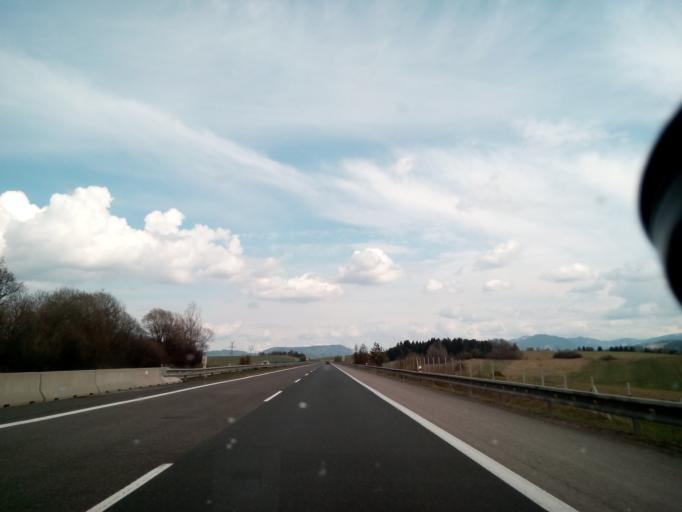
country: SK
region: Zilinsky
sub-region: Okres Zilina
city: Liptovsky Hradok
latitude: 49.0552
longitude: 19.7668
